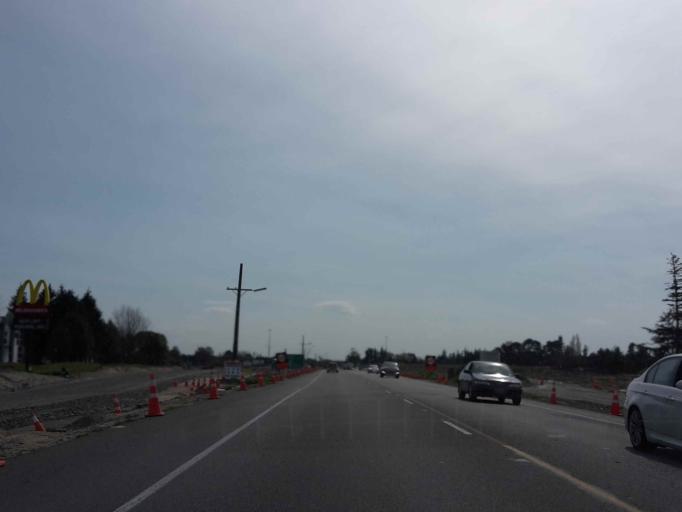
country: NZ
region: Canterbury
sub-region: Selwyn District
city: Prebbleton
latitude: -43.4965
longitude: 172.5479
